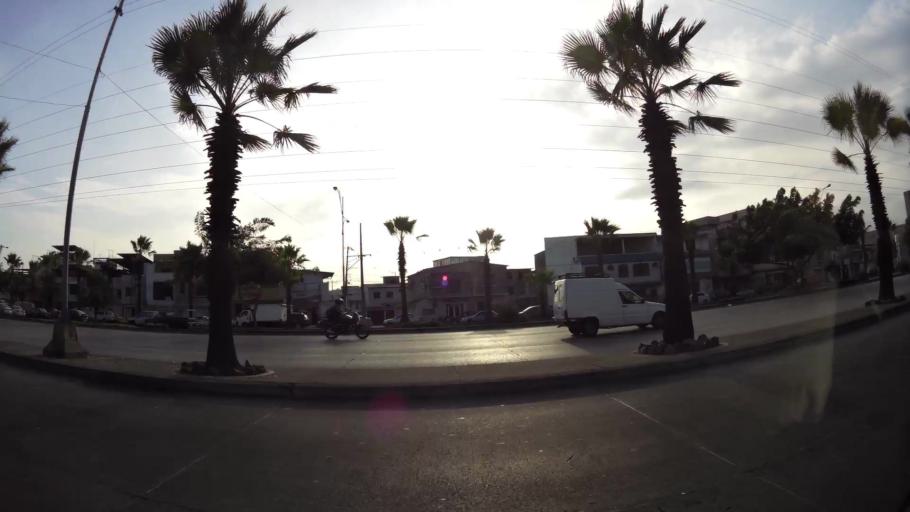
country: EC
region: Guayas
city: Eloy Alfaro
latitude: -2.1308
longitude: -79.9066
